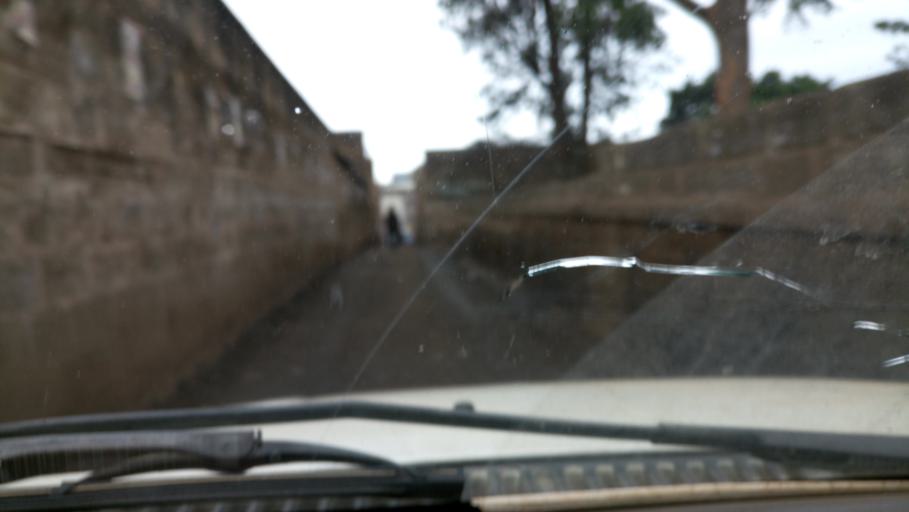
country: KE
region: Nairobi Area
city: Pumwani
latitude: -1.2824
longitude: 36.8362
